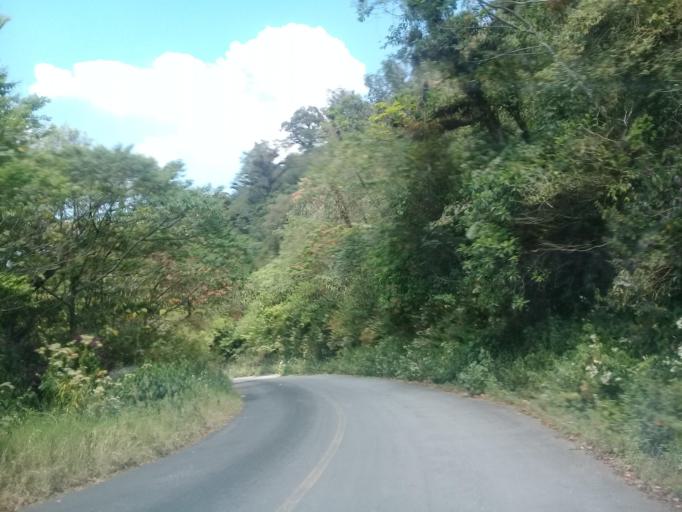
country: MX
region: Veracruz
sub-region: Tlilapan
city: Tonalixco
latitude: 18.8097
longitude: -97.0610
